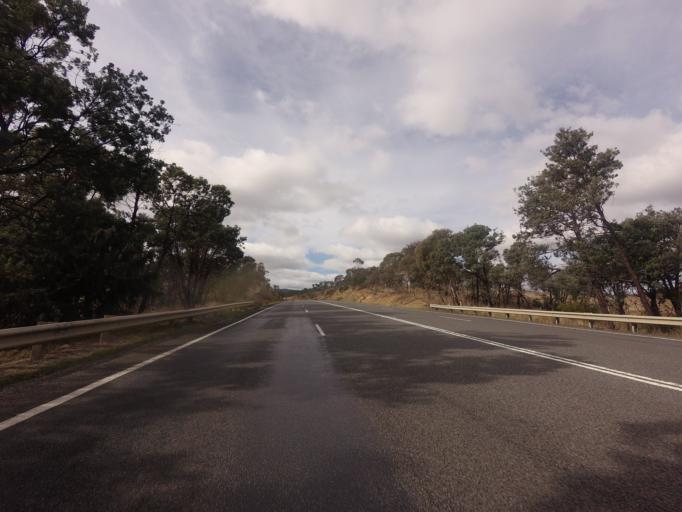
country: AU
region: Tasmania
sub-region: Brighton
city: Bridgewater
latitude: -42.4488
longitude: 147.2095
